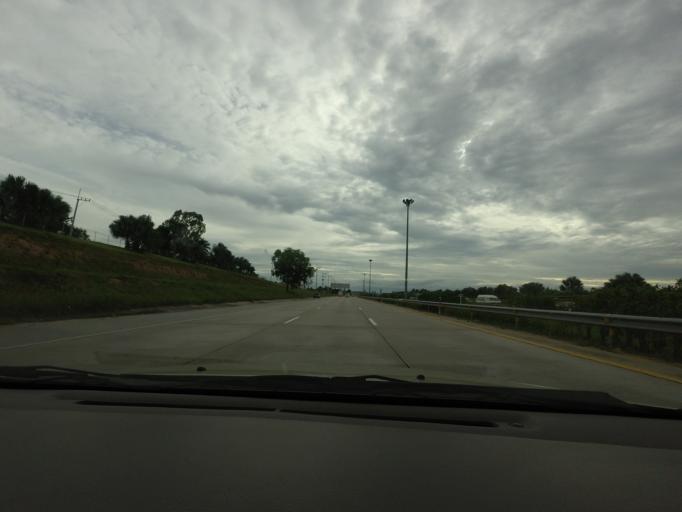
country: TH
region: Chon Buri
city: Phatthaya
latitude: 12.9515
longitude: 100.9627
